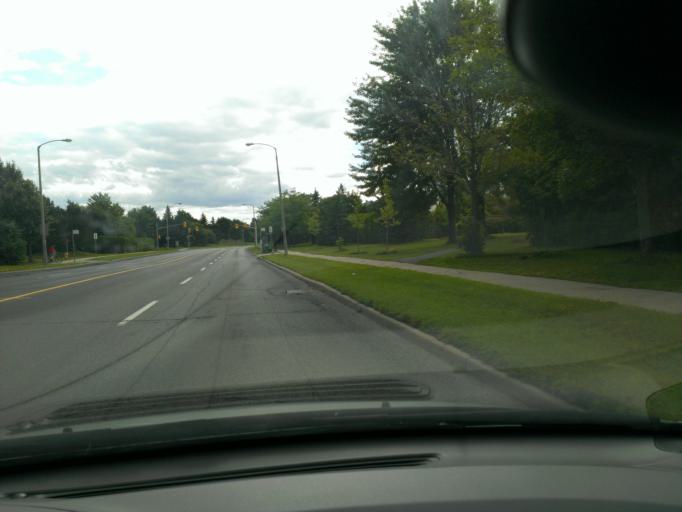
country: CA
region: Ontario
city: Clarence-Rockland
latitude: 45.4776
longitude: -75.4892
